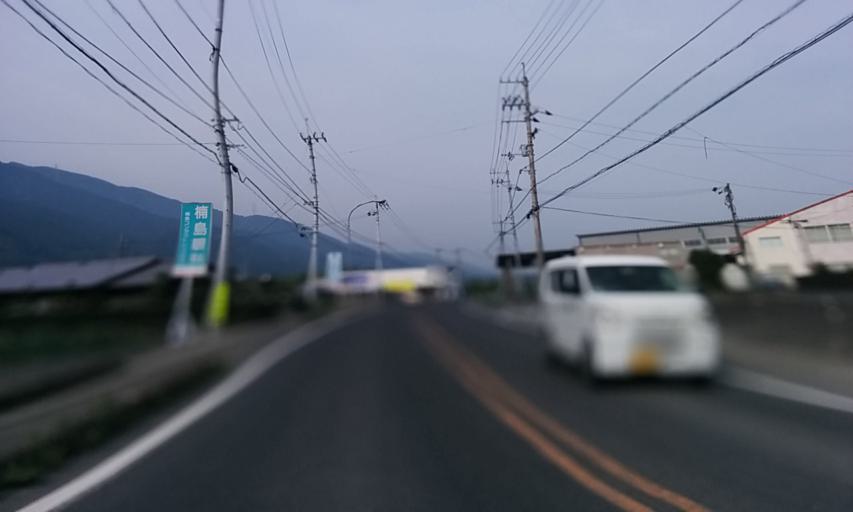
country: JP
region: Ehime
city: Kawanoecho
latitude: 33.9636
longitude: 133.4634
